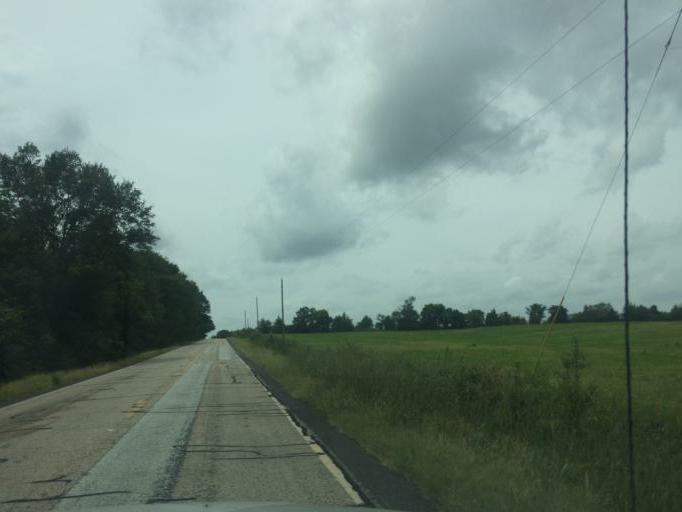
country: US
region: Georgia
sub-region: Hart County
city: Hartwell
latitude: 34.2686
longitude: -82.8808
